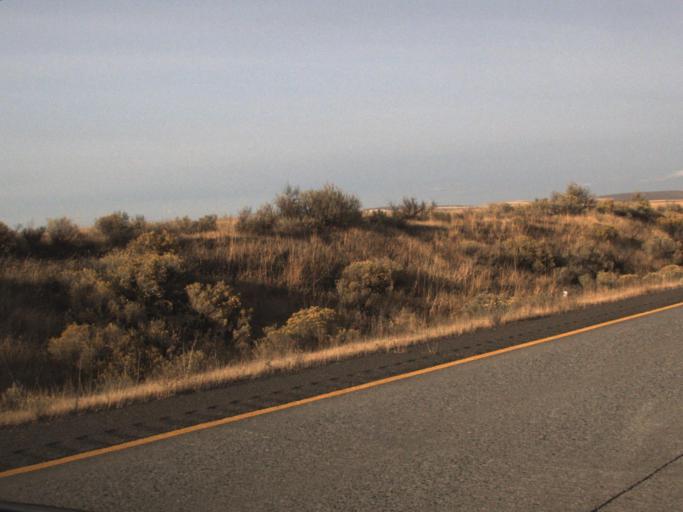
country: US
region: Oregon
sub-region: Umatilla County
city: Umatilla
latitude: 46.0035
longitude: -119.2496
